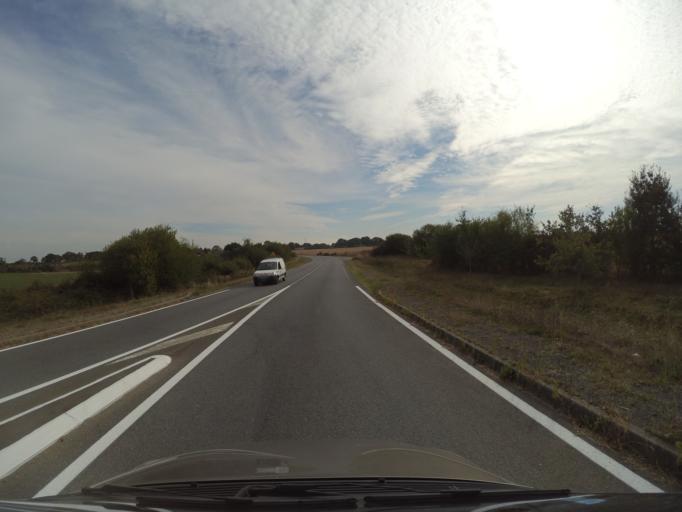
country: FR
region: Pays de la Loire
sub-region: Departement de Maine-et-Loire
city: Chemille-Melay
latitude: 47.2122
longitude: -0.7605
